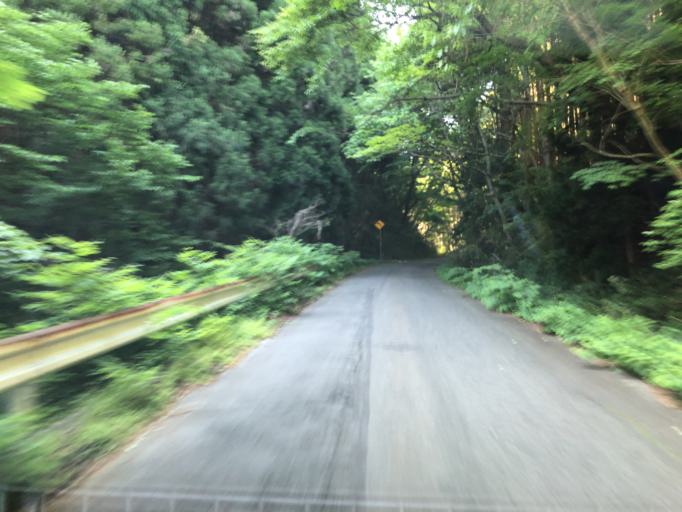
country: JP
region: Ibaraki
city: Kitaibaraki
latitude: 36.8720
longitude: 140.6705
